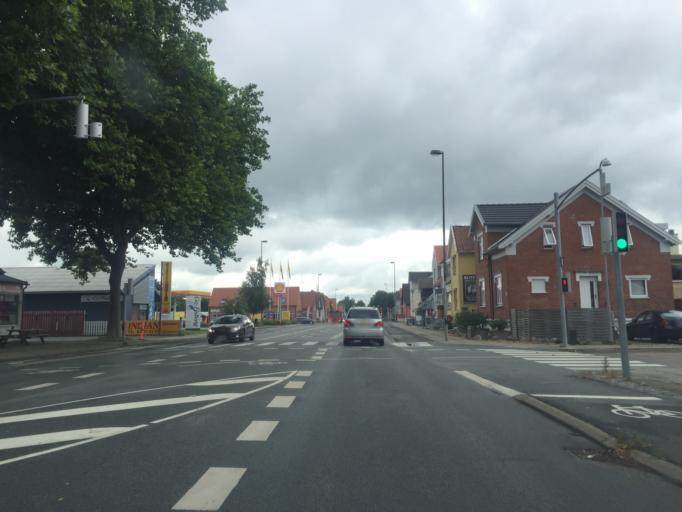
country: DK
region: South Denmark
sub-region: Odense Kommune
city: Odense
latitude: 55.3682
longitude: 10.3725
